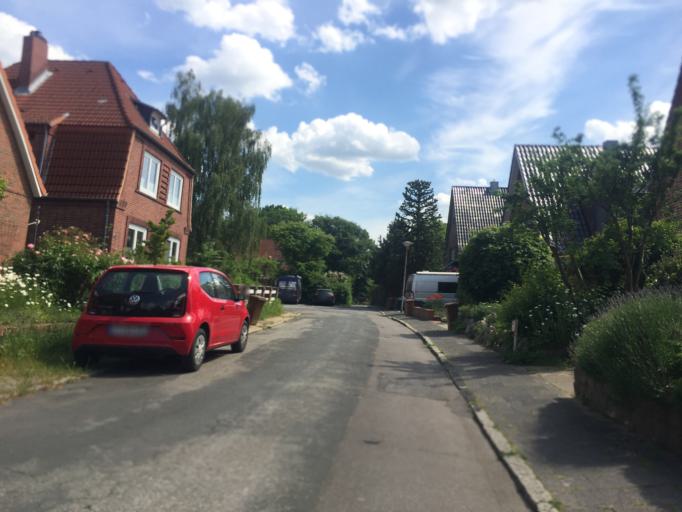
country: DE
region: Schleswig-Holstein
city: Itzehoe
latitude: 53.9287
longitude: 9.5237
